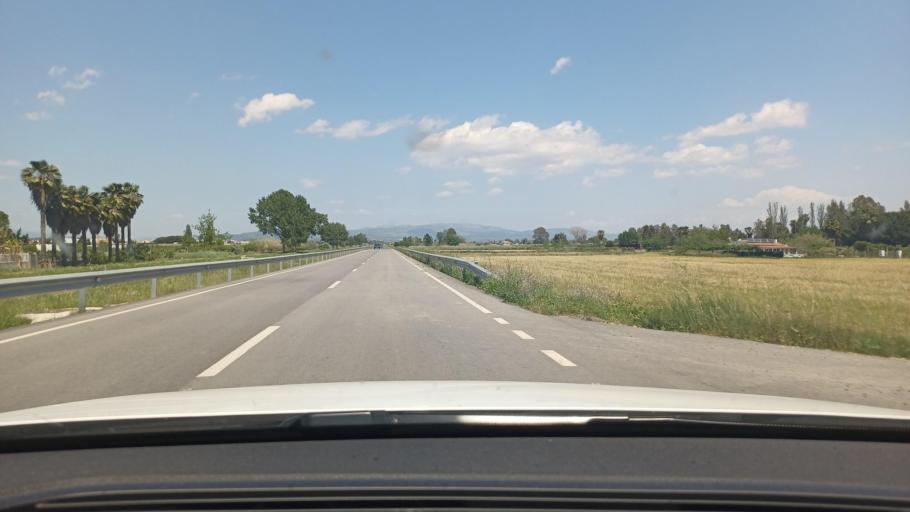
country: ES
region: Catalonia
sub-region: Provincia de Tarragona
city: Amposta
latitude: 40.6761
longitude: 0.5906
